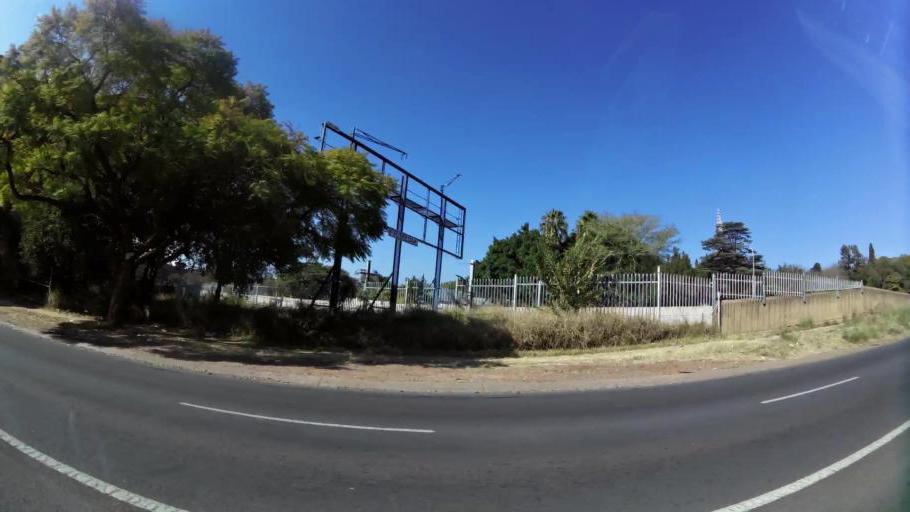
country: ZA
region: Gauteng
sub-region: City of Tshwane Metropolitan Municipality
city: Pretoria
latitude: -25.7606
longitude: 28.1998
